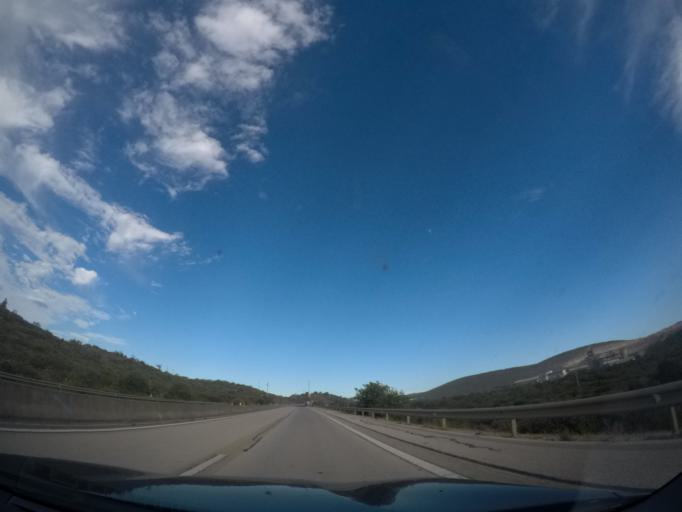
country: PT
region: Faro
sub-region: Loule
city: Vilamoura
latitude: 37.1296
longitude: -8.0978
